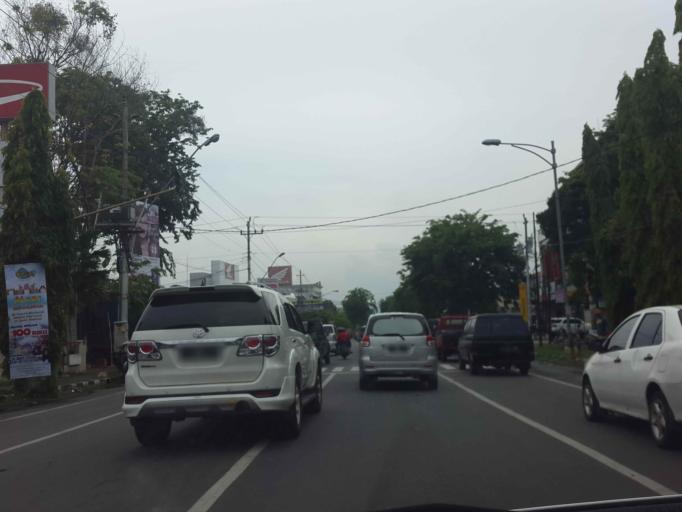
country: ID
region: Central Java
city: Semarang
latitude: -6.9847
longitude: 110.4348
